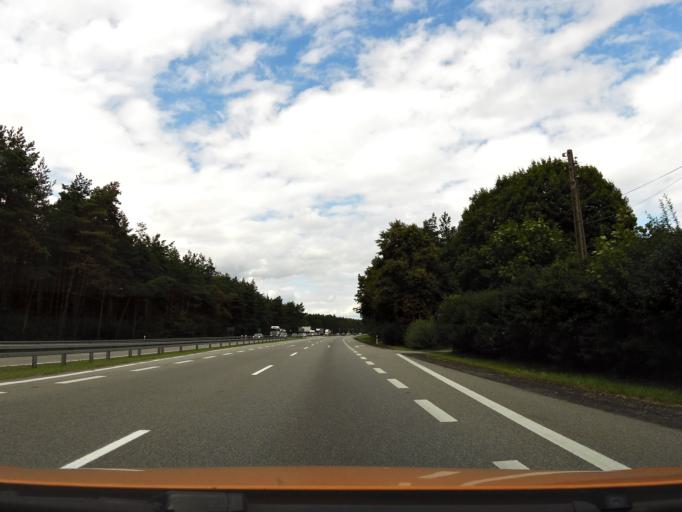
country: PL
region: West Pomeranian Voivodeship
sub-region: Powiat goleniowski
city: Goleniow
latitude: 53.4663
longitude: 14.7876
